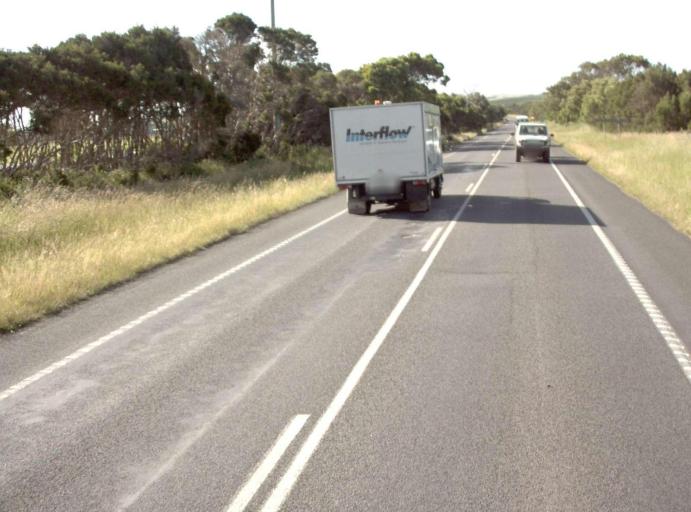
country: AU
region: Victoria
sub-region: Bass Coast
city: North Wonthaggi
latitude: -38.5751
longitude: 145.5712
